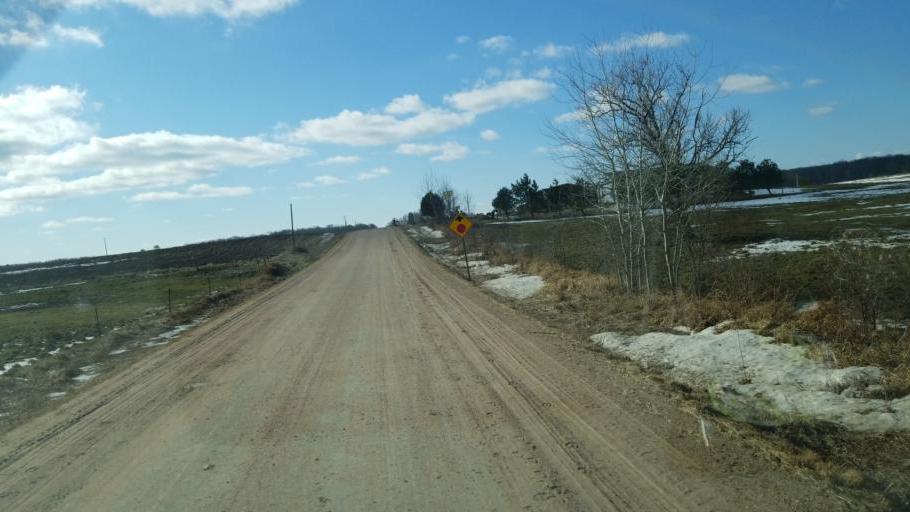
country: US
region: Wisconsin
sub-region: Clark County
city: Loyal
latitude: 44.6283
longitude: -90.3970
